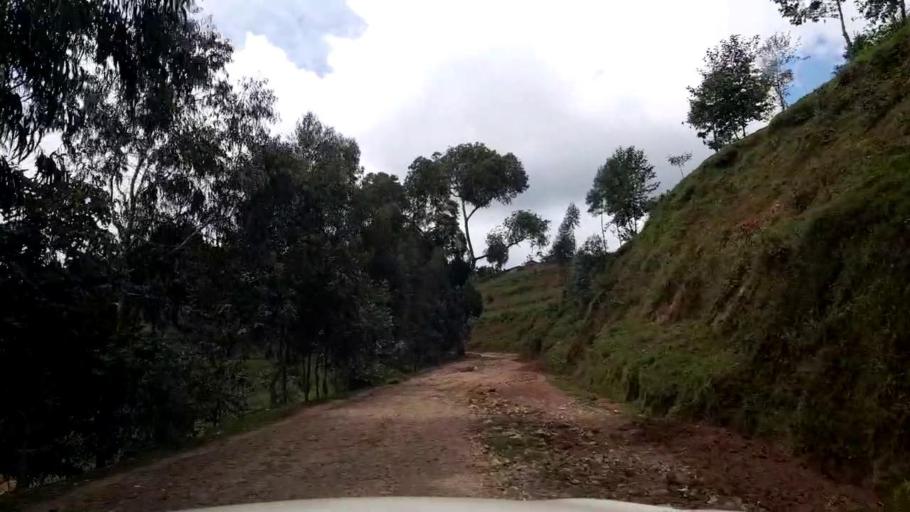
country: RW
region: Western Province
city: Kibuye
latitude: -1.9034
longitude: 29.4540
